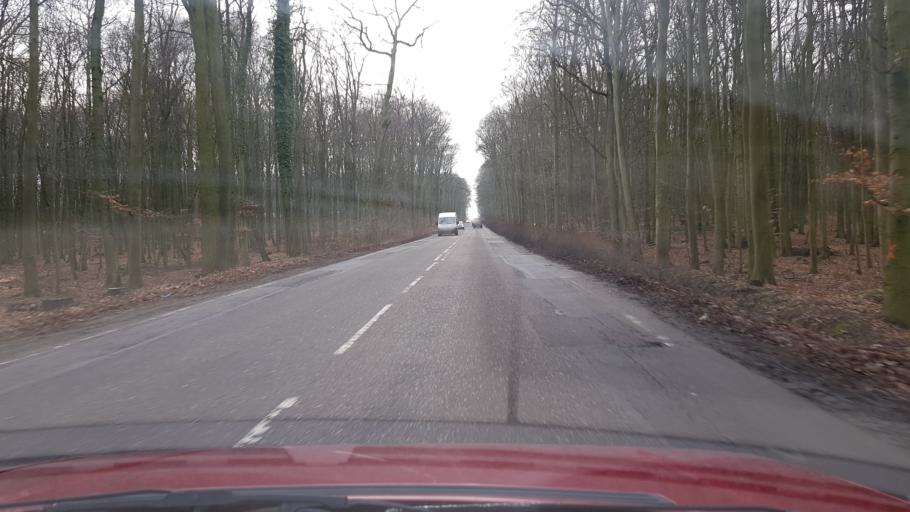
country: PL
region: West Pomeranian Voivodeship
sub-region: Powiat policki
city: Police
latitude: 53.5315
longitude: 14.5749
